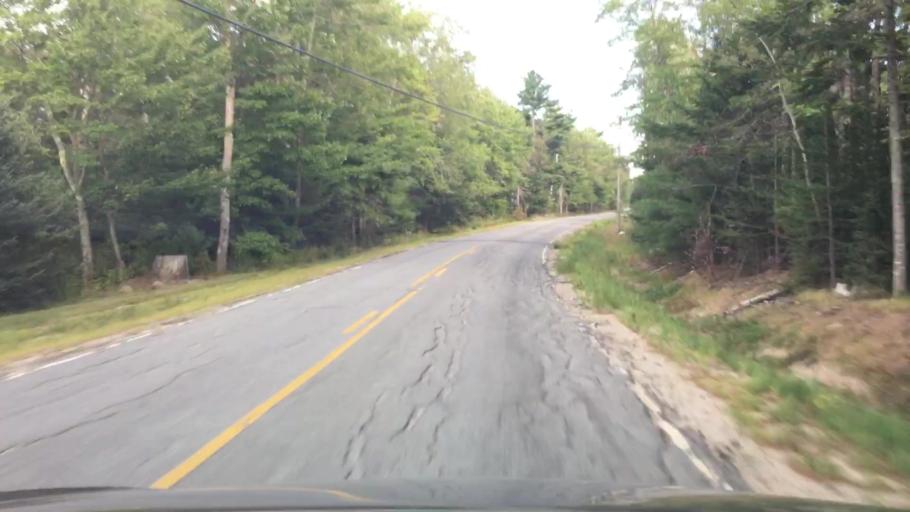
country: US
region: Maine
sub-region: Hancock County
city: Surry
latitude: 44.4992
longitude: -68.5485
